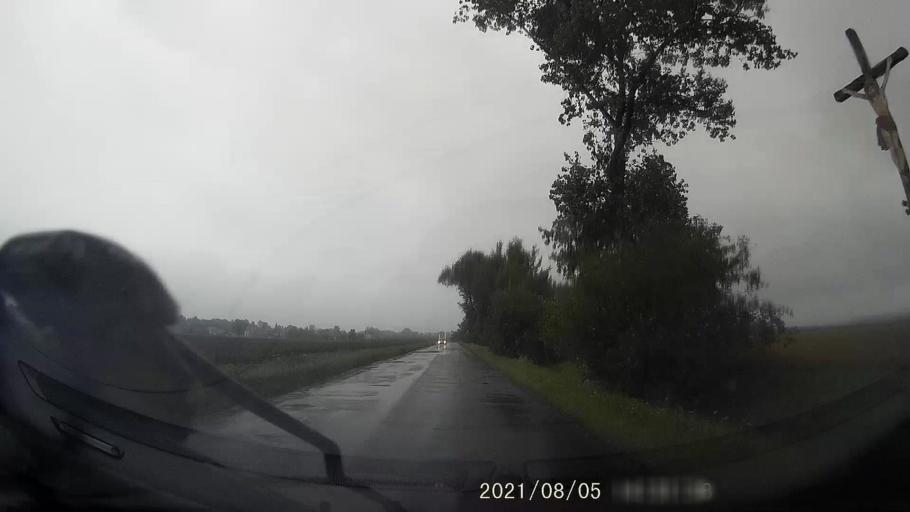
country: PL
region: Opole Voivodeship
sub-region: Powiat nyski
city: Korfantow
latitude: 50.4732
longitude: 17.5554
